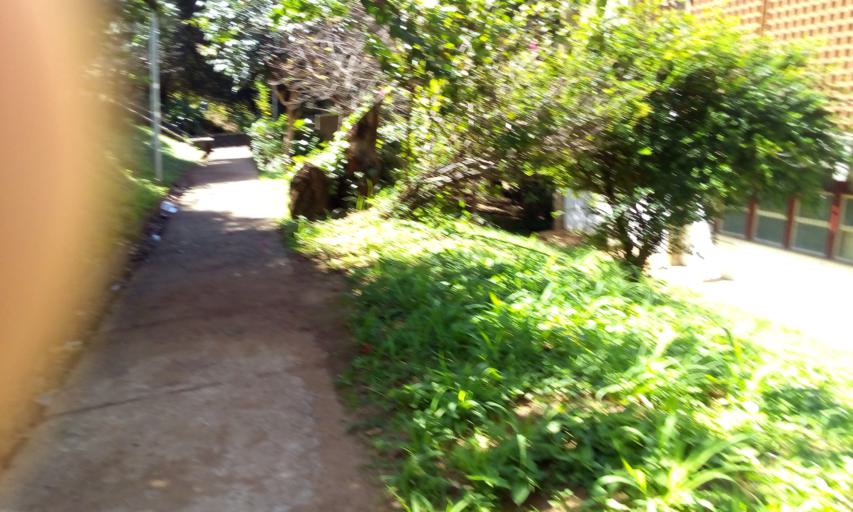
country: BR
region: Bahia
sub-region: Salvador
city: Salvador
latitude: -12.9945
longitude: -38.5208
